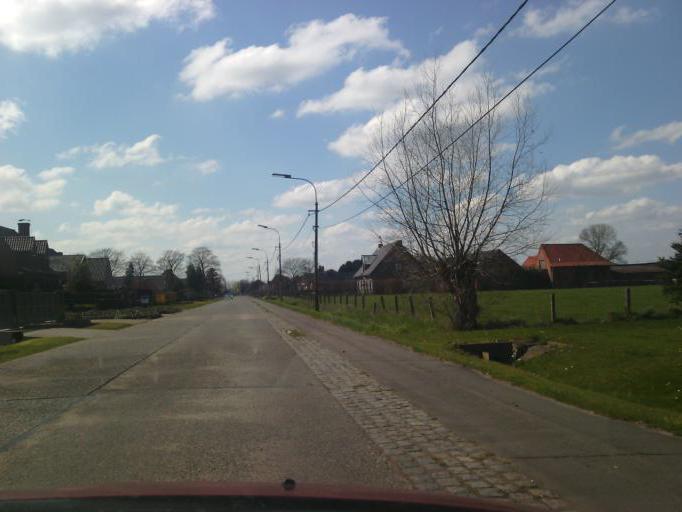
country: BE
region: Flanders
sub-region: Provincie Oost-Vlaanderen
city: Lokeren
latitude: 51.0848
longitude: 3.9253
